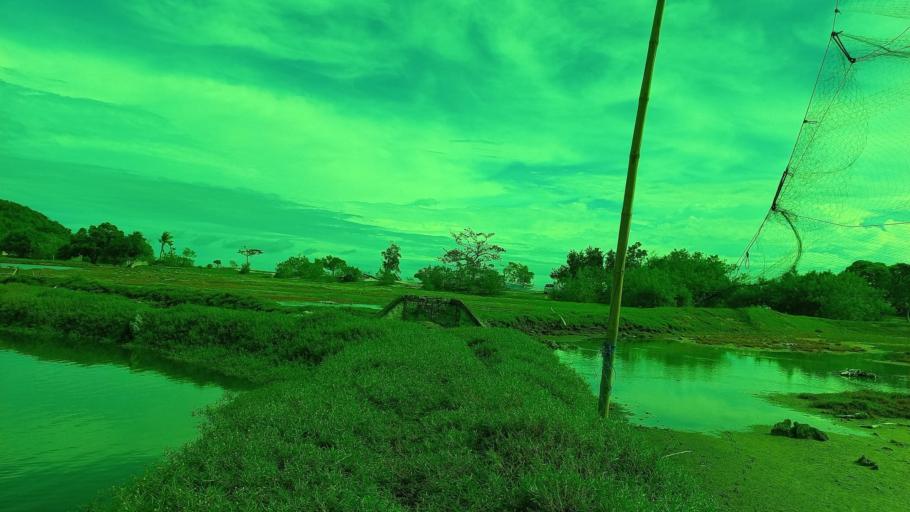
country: PH
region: Central Visayas
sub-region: Province of Siquijor
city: Lazi
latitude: 9.1255
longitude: 123.6483
